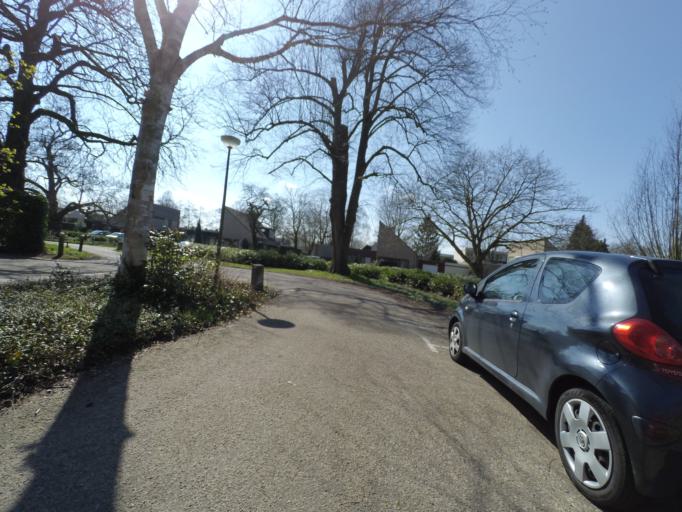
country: NL
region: Utrecht
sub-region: Gemeente Utrechtse Heuvelrug
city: Driebergen-Rijsenburg
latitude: 52.0528
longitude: 5.2731
